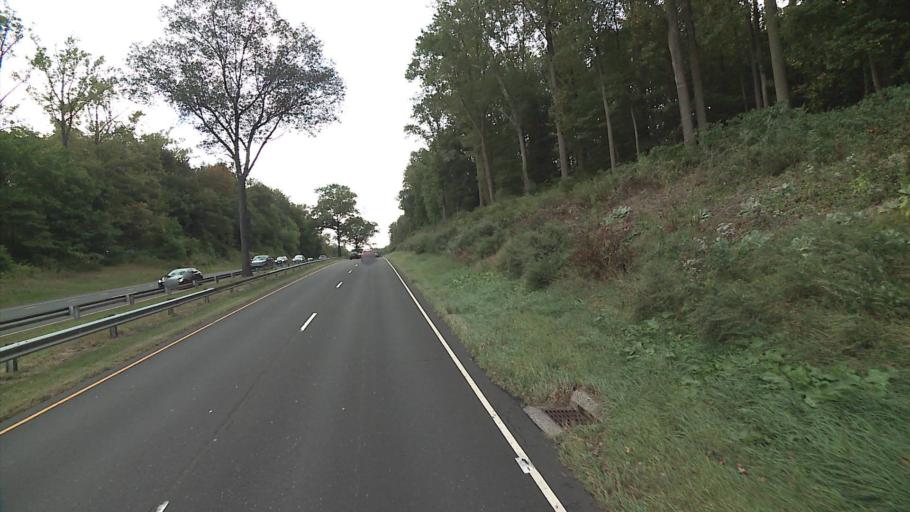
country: US
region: Connecticut
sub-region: Fairfield County
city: New Canaan
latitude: 41.1308
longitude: -73.4612
